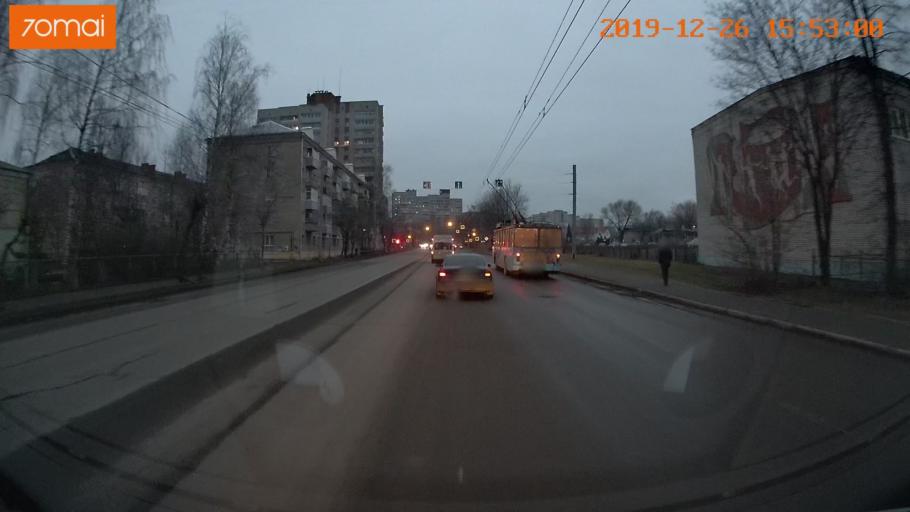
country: RU
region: Jaroslavl
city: Rybinsk
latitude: 58.0493
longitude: 38.8235
